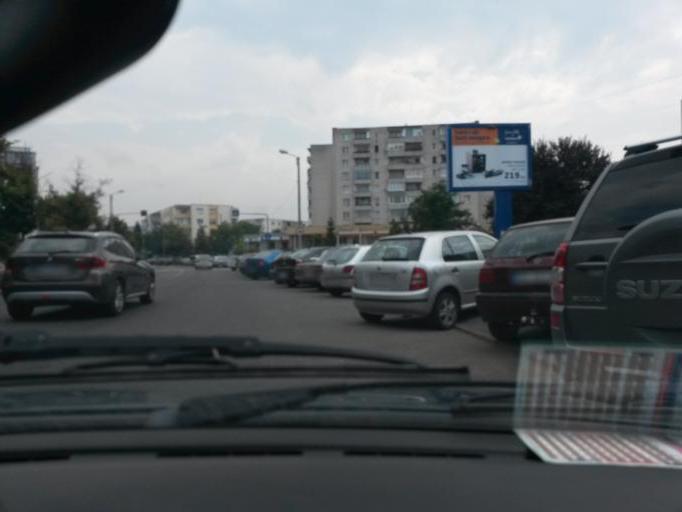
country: RO
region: Mures
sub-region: Comuna Corunca
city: Corunca
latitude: 46.5367
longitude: 24.5914
